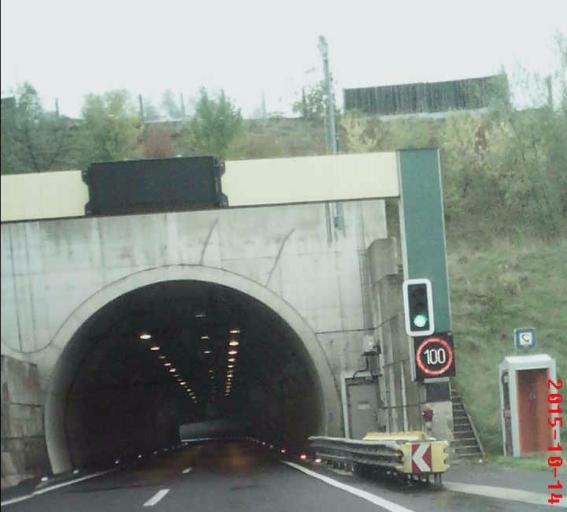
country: AT
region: Upper Austria
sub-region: Politischer Bezirk Kirchdorf an der Krems
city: Micheldorf in Oberoesterreich
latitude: 47.9177
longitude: 14.1017
